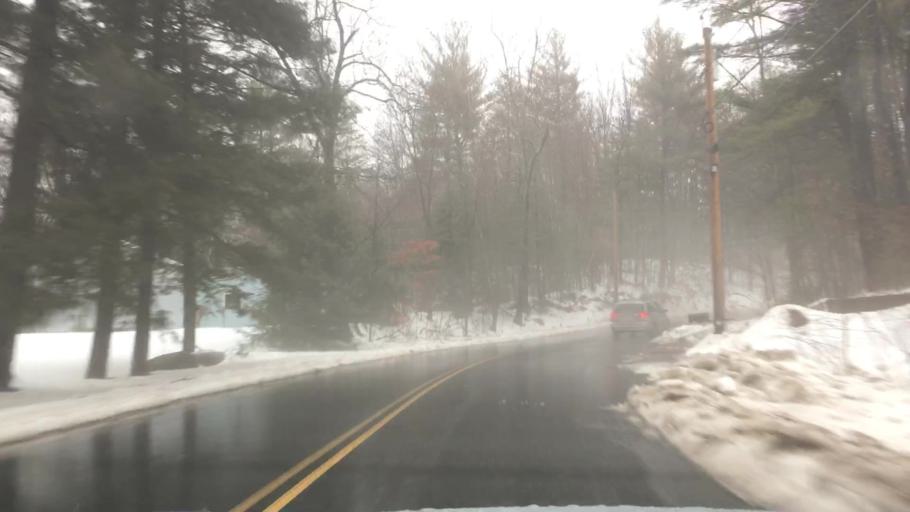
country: US
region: Massachusetts
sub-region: Hampshire County
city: Granby
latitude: 42.2495
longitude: -72.4738
